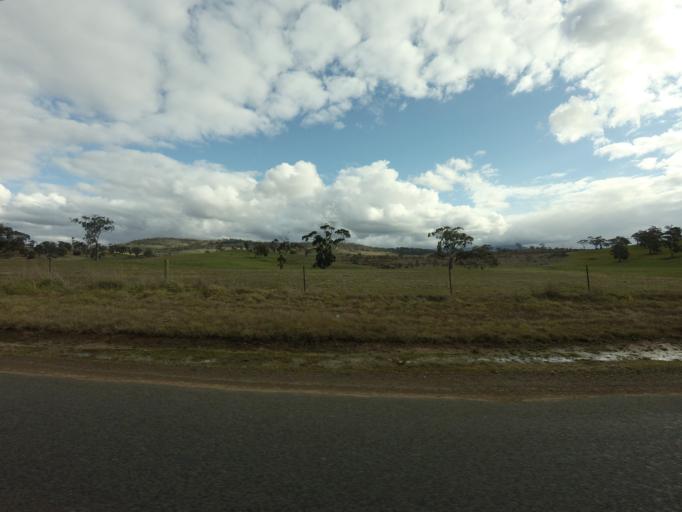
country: AU
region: Tasmania
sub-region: Northern Midlands
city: Evandale
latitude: -41.8826
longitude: 147.3093
